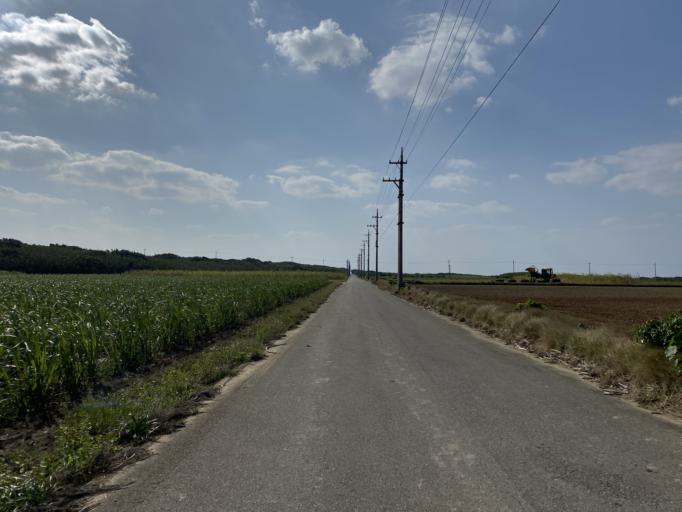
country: JP
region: Okinawa
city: Ishigaki
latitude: 24.0652
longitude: 123.7924
